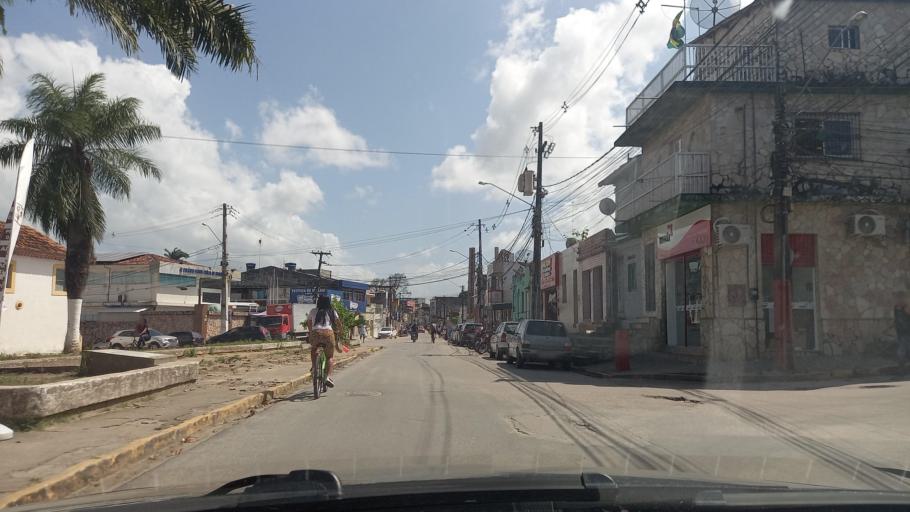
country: BR
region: Pernambuco
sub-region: Goiana
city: Goiana
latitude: -7.5619
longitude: -35.0018
